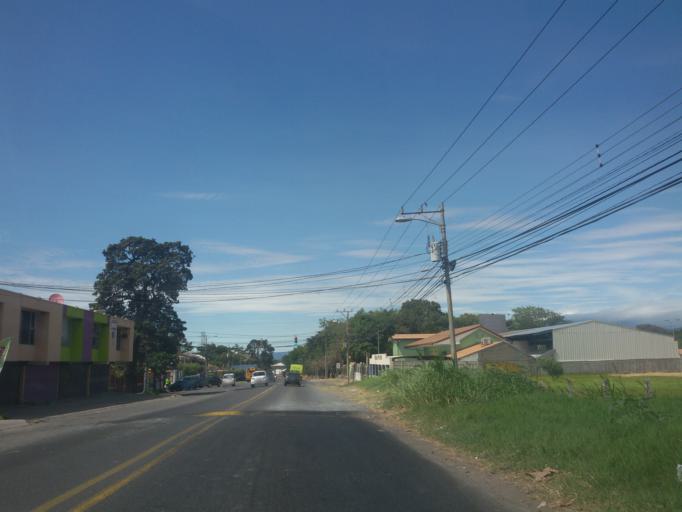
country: CR
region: San Jose
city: San Rafael
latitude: 9.9583
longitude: -84.1198
